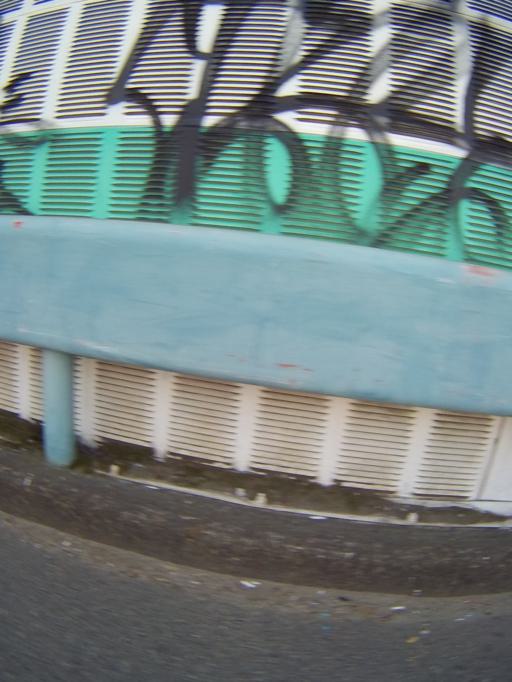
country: JP
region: Osaka
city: Osaka-shi
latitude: 34.6778
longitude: 135.4567
